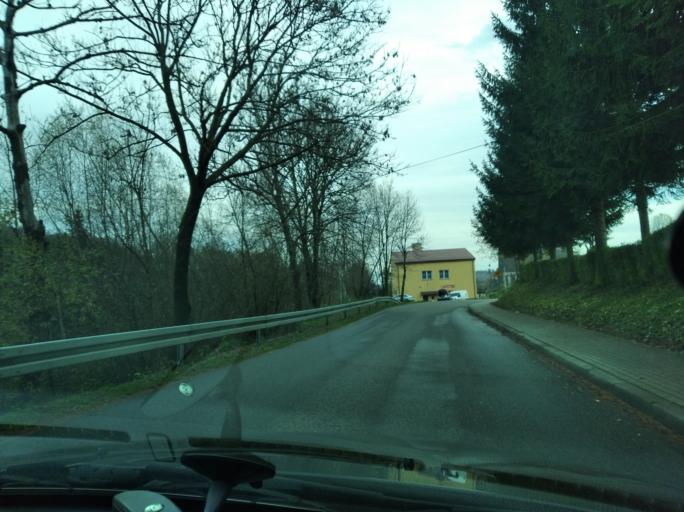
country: PL
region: Subcarpathian Voivodeship
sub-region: Powiat strzyzowski
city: Strzyzow
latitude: 49.9350
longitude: 21.7613
